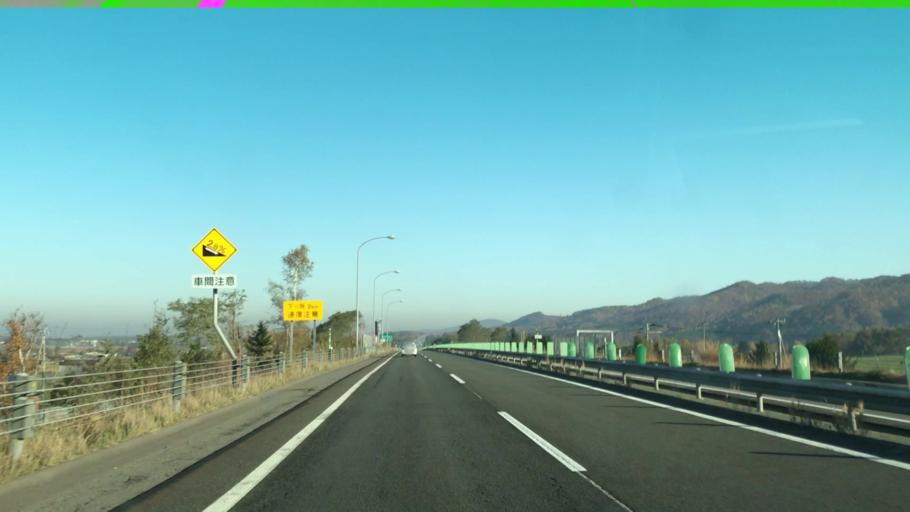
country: JP
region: Hokkaido
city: Sunagawa
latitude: 43.4371
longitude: 141.9157
